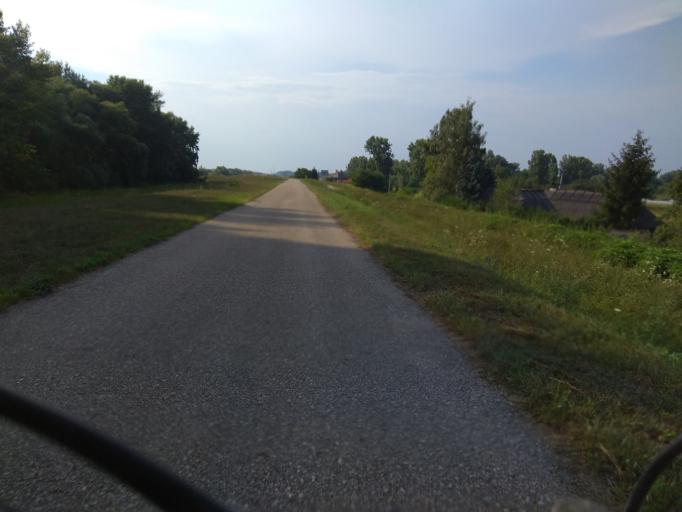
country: SK
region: Trnavsky
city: Gabcikovo
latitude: 47.8204
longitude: 17.6135
